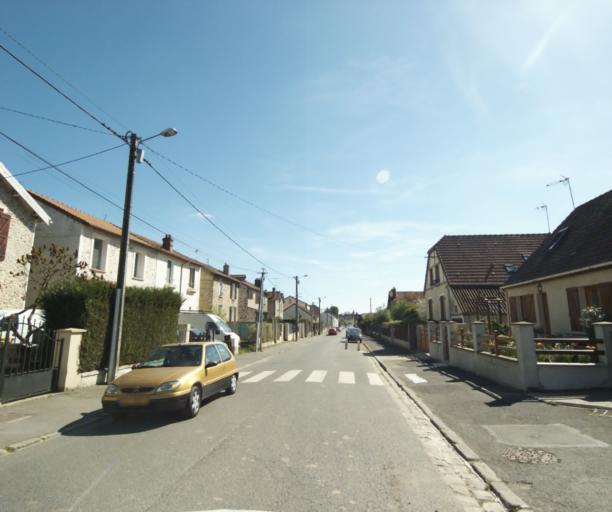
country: FR
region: Ile-de-France
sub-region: Departement de Seine-et-Marne
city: Nangis
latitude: 48.5643
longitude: 3.0130
